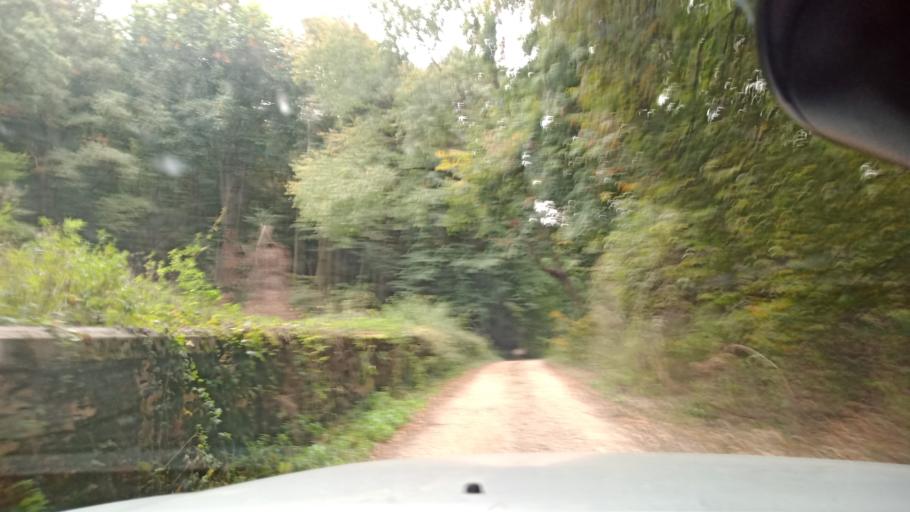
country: HU
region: Fejer
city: Pusztavam
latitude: 47.3931
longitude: 18.2623
